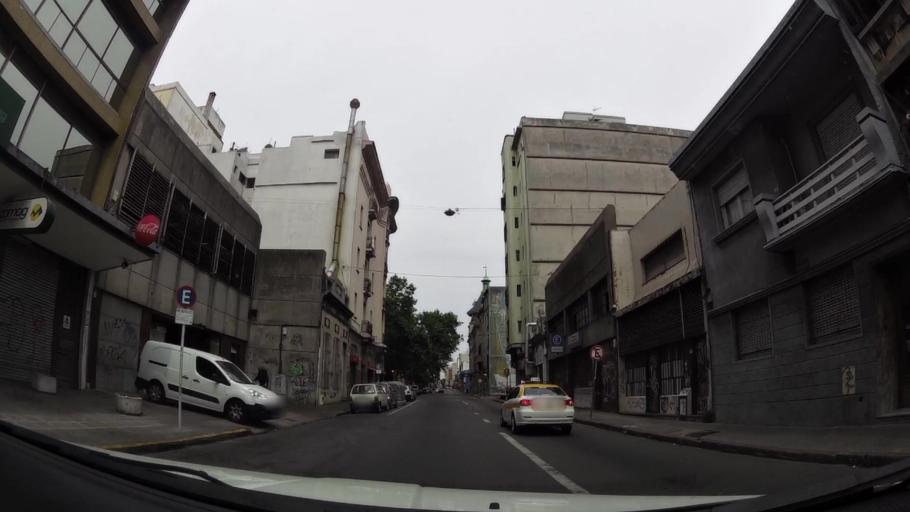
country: UY
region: Montevideo
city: Montevideo
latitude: -34.9022
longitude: -56.1796
